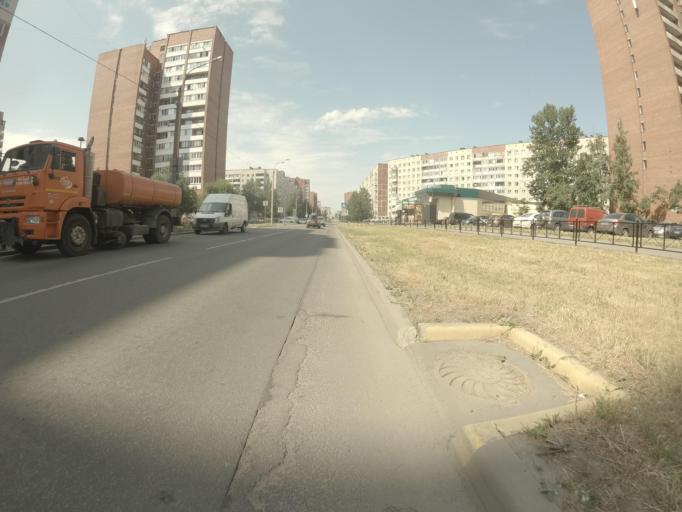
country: RU
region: St.-Petersburg
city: Krasnogvargeisky
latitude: 59.9401
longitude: 30.4955
